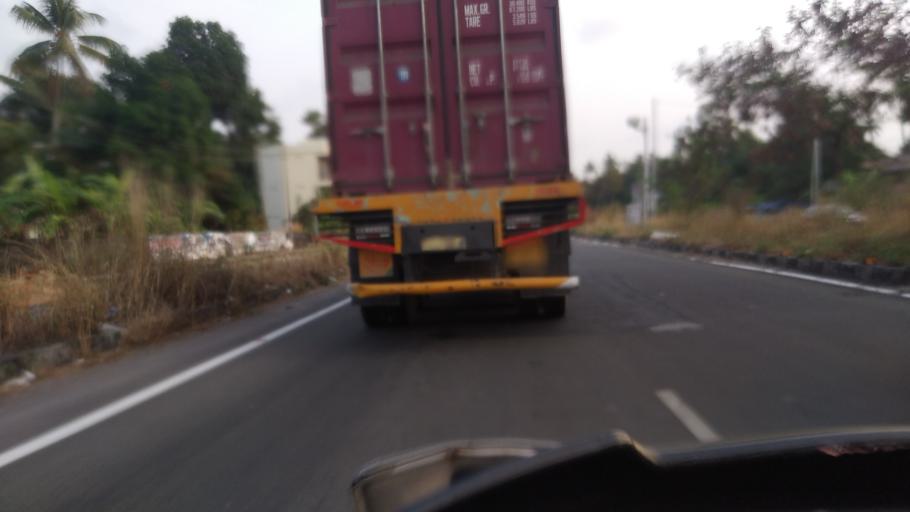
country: IN
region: Kerala
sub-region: Thrissur District
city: Kodungallur
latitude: 10.2300
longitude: 76.1954
